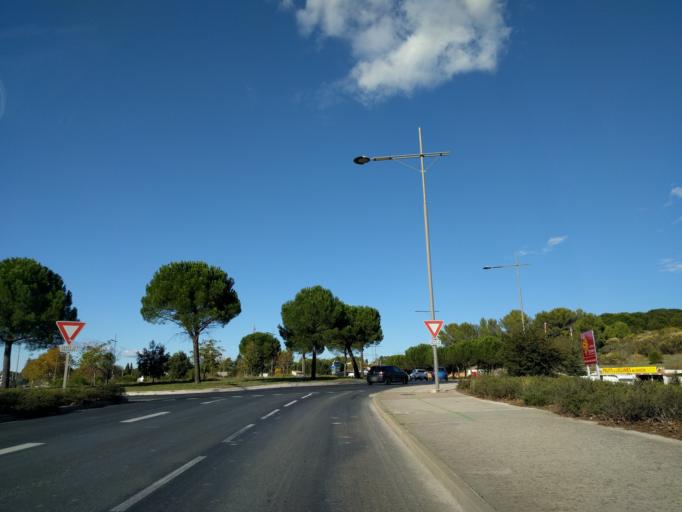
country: FR
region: Languedoc-Roussillon
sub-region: Departement de l'Herault
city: Montferrier-sur-Lez
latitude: 43.6402
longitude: 3.8476
